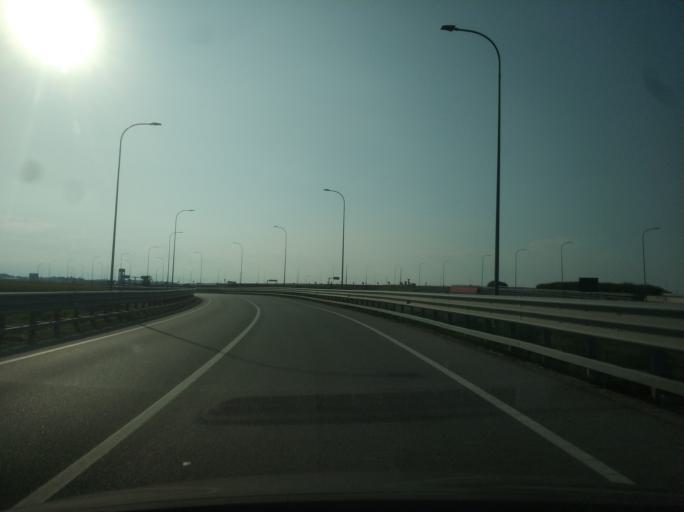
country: IT
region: Piedmont
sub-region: Provincia di Cuneo
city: Roreto
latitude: 44.6631
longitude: 7.8117
